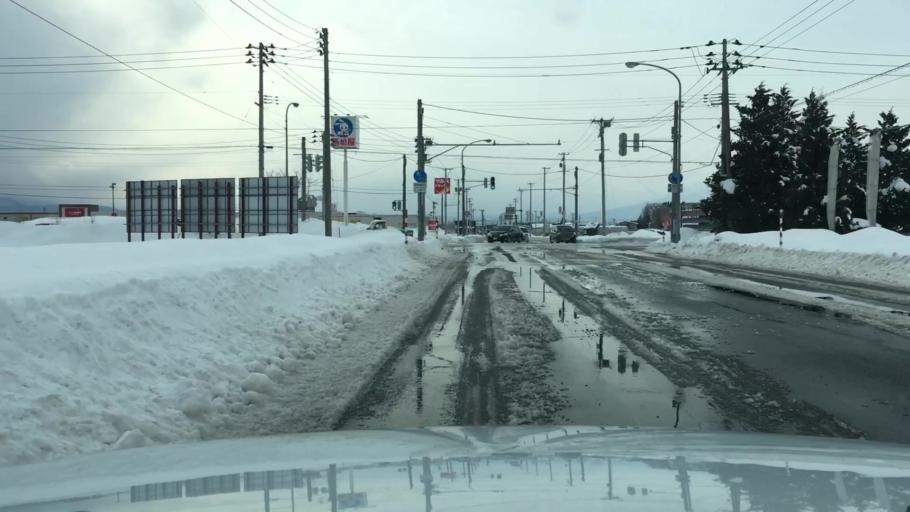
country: JP
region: Aomori
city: Kuroishi
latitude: 40.5917
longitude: 140.5698
